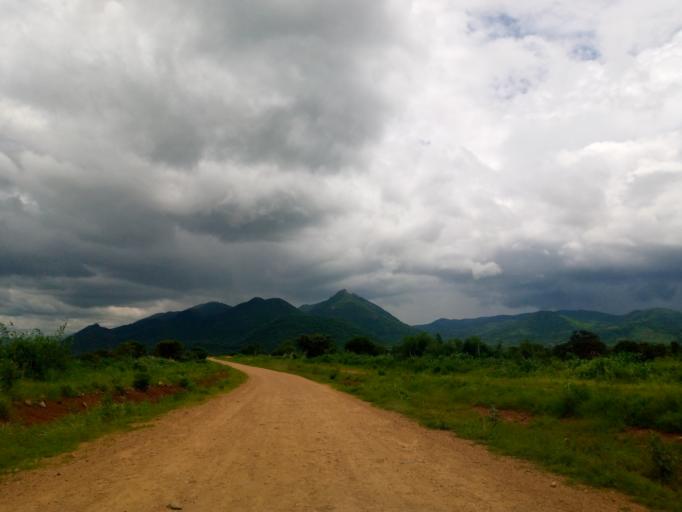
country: ET
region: Oromiya
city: Mendi
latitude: 10.1888
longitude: 35.0933
